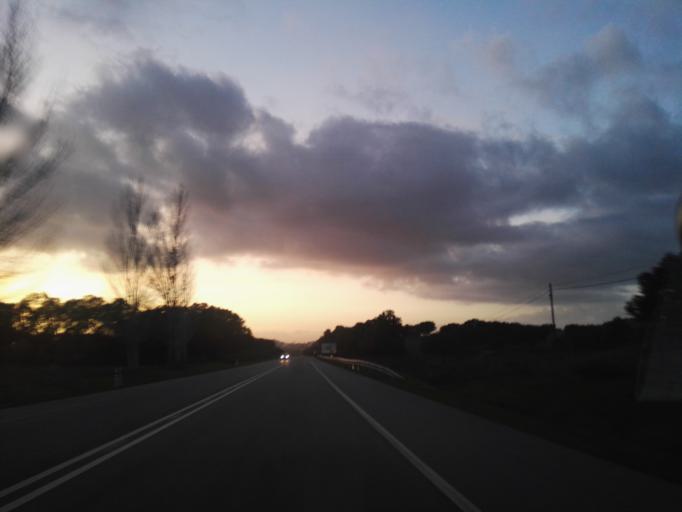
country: PT
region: Evora
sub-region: Montemor-O-Novo
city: Montemor-o-Novo
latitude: 38.6442
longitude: -8.1817
